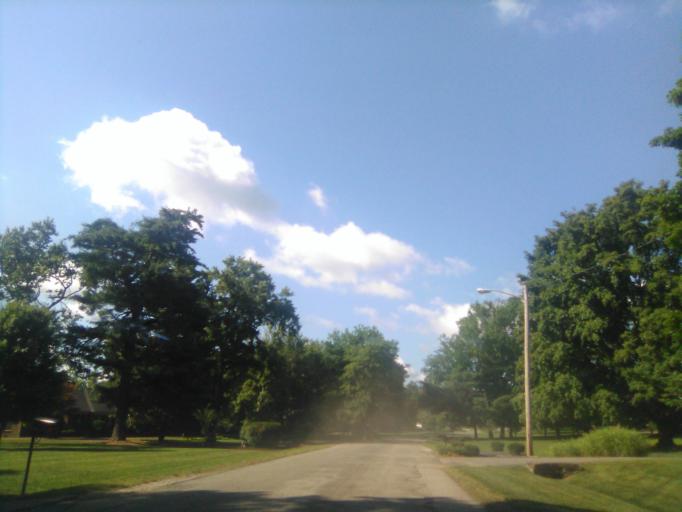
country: US
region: Tennessee
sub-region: Davidson County
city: Belle Meade
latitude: 36.1125
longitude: -86.8692
